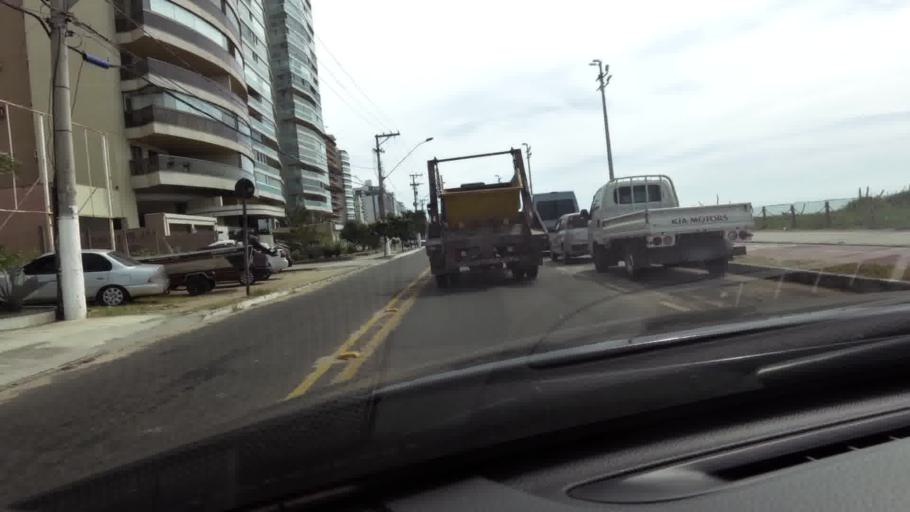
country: BR
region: Espirito Santo
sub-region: Vila Velha
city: Vila Velha
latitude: -20.3770
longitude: -40.3058
